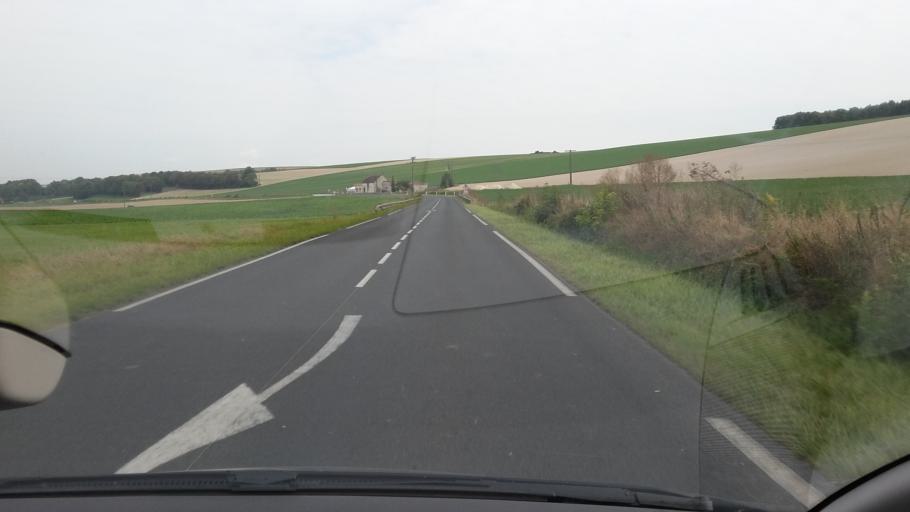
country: FR
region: Champagne-Ardenne
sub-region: Departement de la Marne
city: Mareuil-sur-Ay
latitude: 49.0798
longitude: 4.0765
